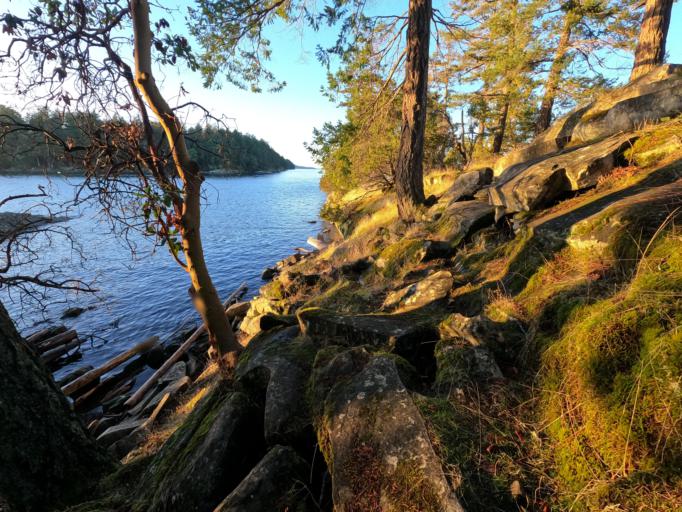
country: CA
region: British Columbia
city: North Cowichan
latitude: 48.9558
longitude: -123.5733
